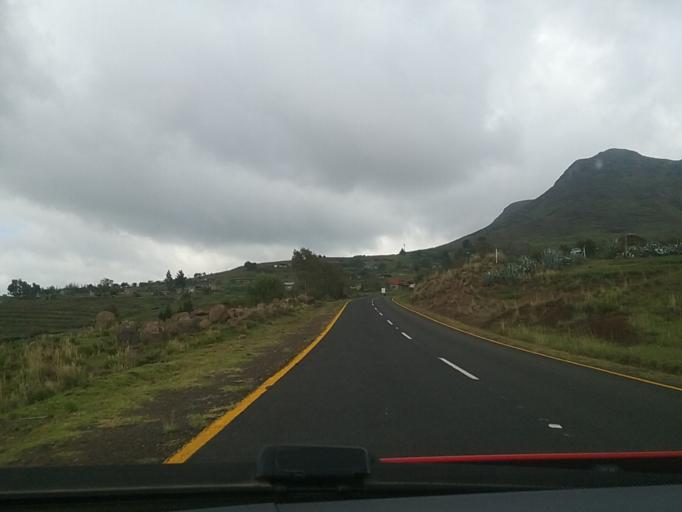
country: LS
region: Berea
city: Teyateyaneng
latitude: -29.2482
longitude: 27.8479
